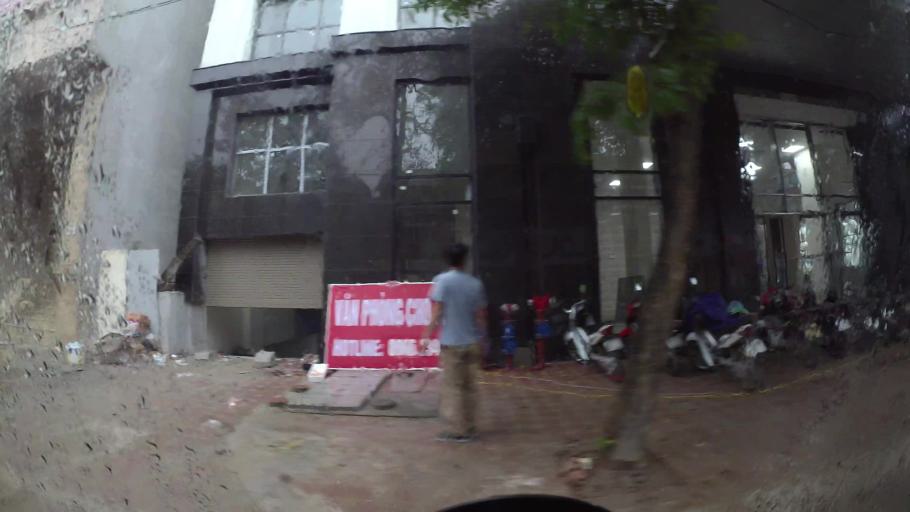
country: VN
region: Ha Noi
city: Hai BaTrung
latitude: 21.0157
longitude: 105.8531
